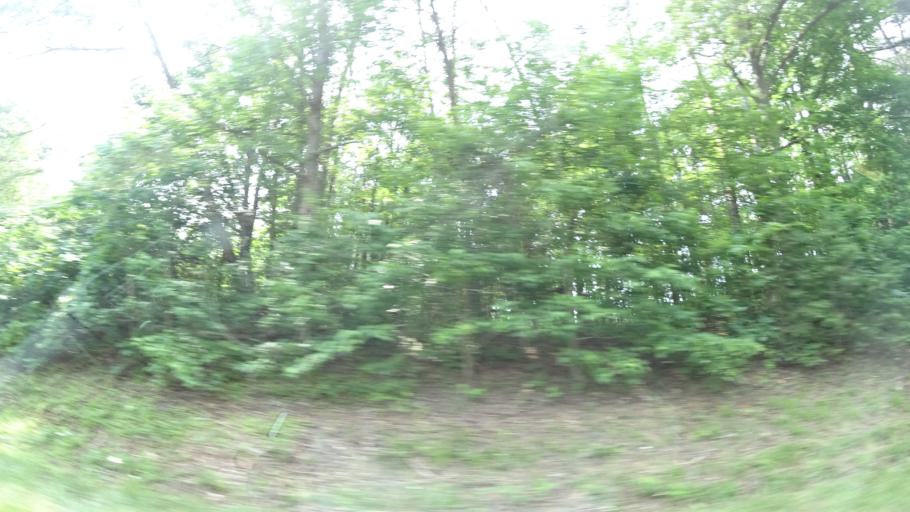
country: US
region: Virginia
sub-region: Spotsylvania County
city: Spotsylvania Courthouse
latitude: 38.1209
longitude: -77.7429
